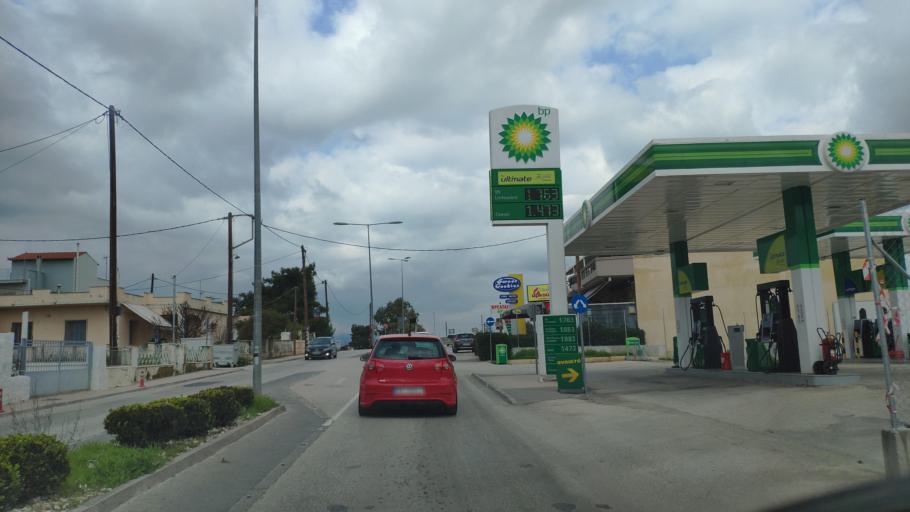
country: GR
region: Peloponnese
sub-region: Nomos Argolidos
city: Argos
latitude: 37.6452
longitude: 22.7291
